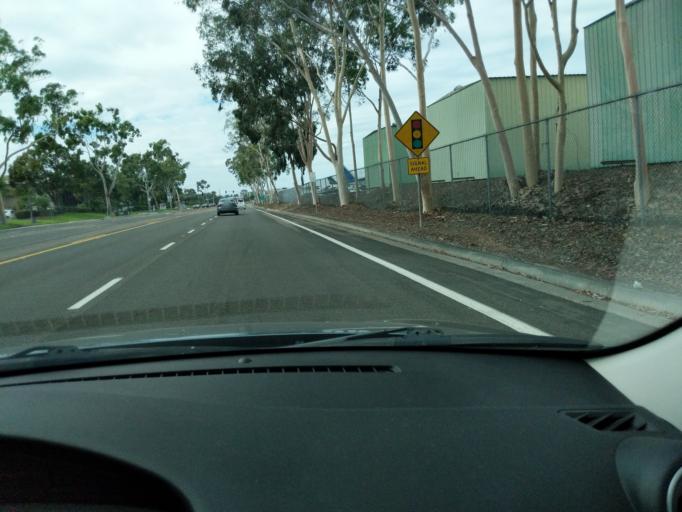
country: US
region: California
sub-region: San Diego County
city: San Diego
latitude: 32.8099
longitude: -117.1372
